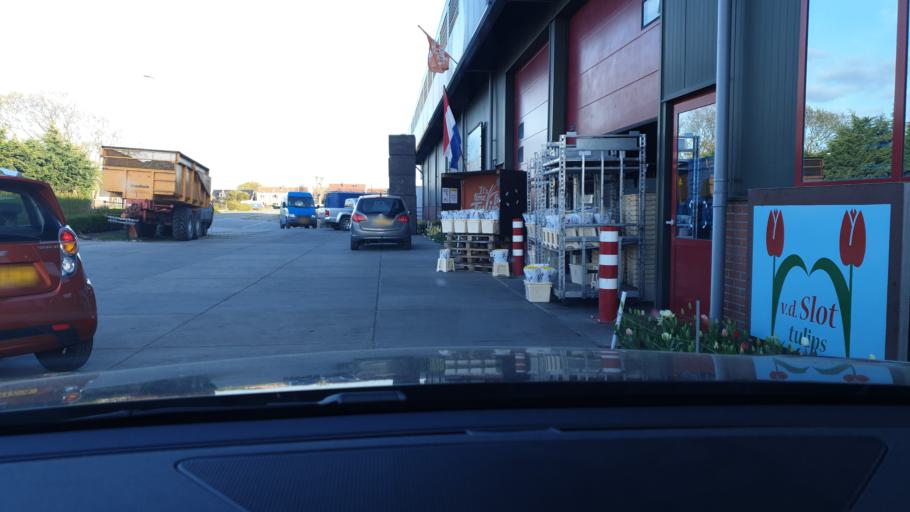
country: NL
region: South Holland
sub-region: Gemeente Teylingen
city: Sassenheim
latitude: 52.2445
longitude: 4.5208
